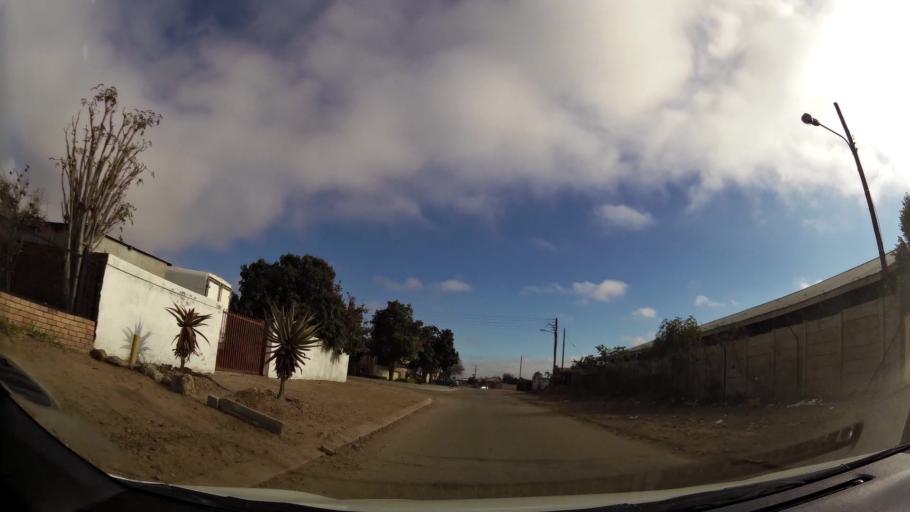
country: ZA
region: Limpopo
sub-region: Capricorn District Municipality
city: Polokwane
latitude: -23.8478
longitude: 29.3857
